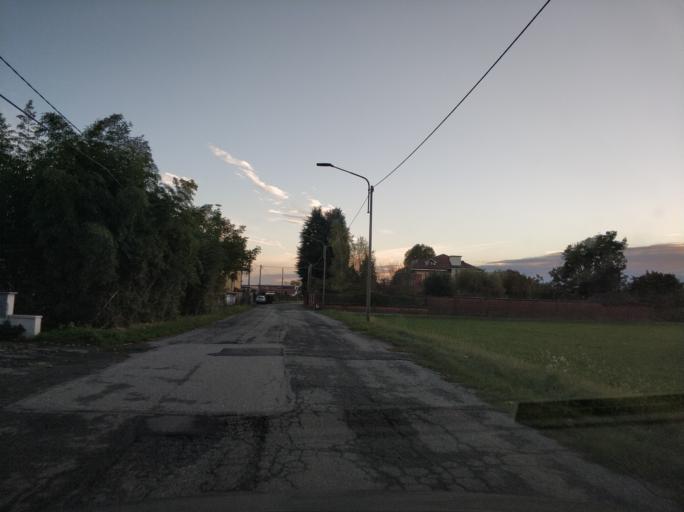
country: IT
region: Piedmont
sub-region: Provincia di Torino
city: Cirie
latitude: 45.2277
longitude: 7.5927
